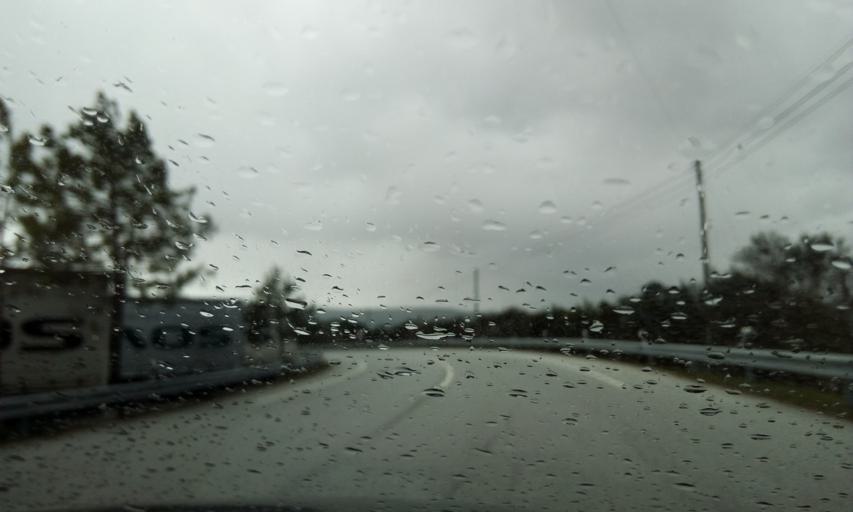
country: PT
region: Guarda
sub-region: Fornos de Algodres
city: Fornos de Algodres
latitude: 40.6188
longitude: -7.6139
